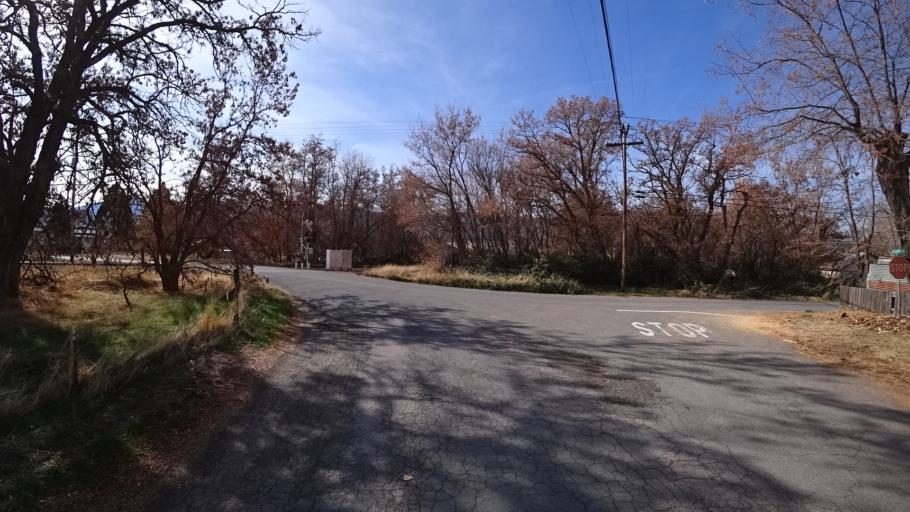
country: US
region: California
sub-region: Siskiyou County
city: Weed
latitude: 41.4586
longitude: -122.4323
